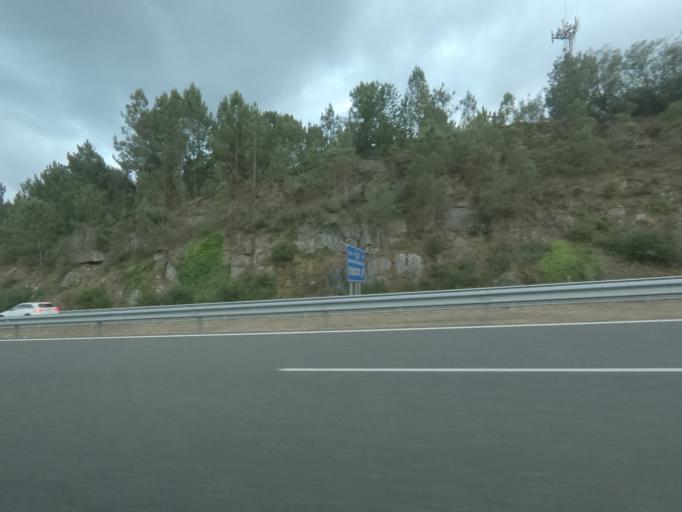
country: ES
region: Galicia
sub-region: Provincia de Ourense
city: Ribadavia
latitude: 42.3024
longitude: -8.1407
